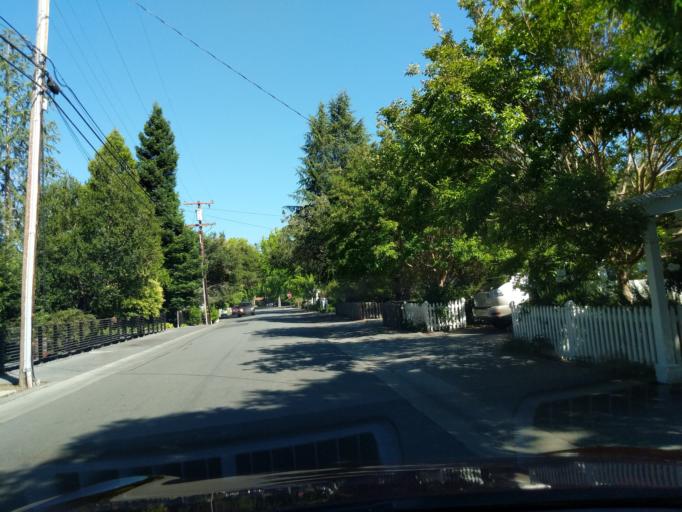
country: US
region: California
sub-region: San Mateo County
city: Menlo Park
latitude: 37.4396
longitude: -122.1879
